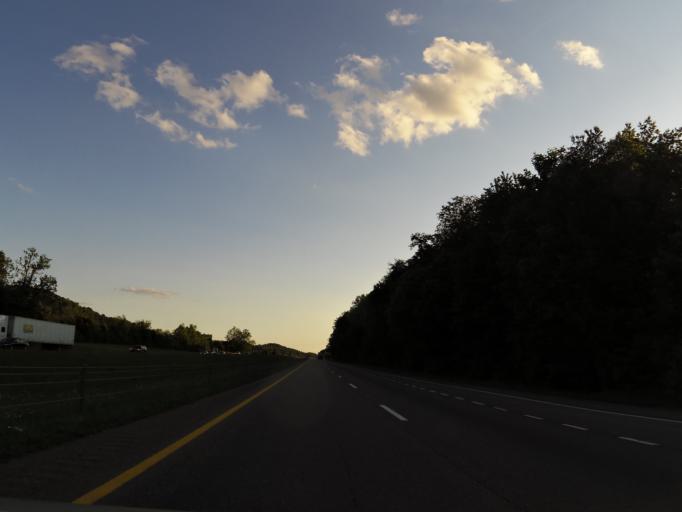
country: US
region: Tennessee
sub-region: Sullivan County
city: Blountville
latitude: 36.5301
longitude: -82.3924
